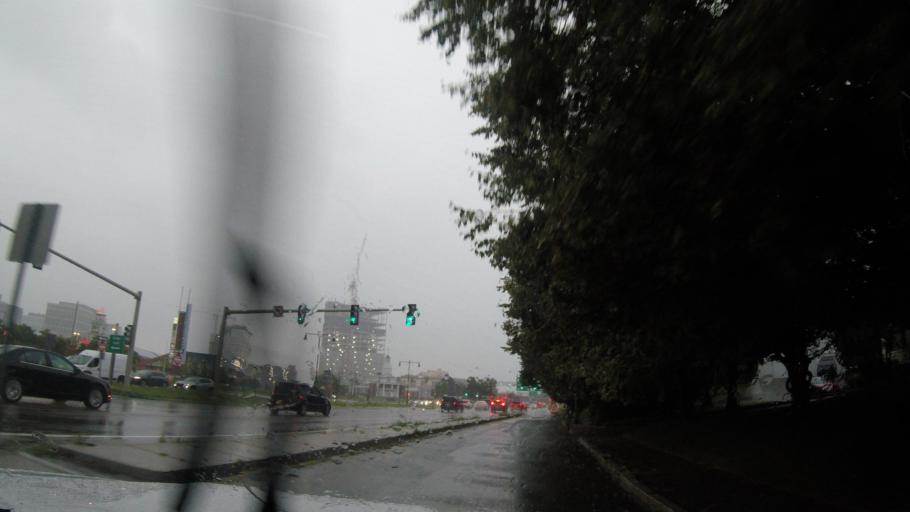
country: US
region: Massachusetts
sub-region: Middlesex County
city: Somerville
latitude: 42.3978
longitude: -71.0848
